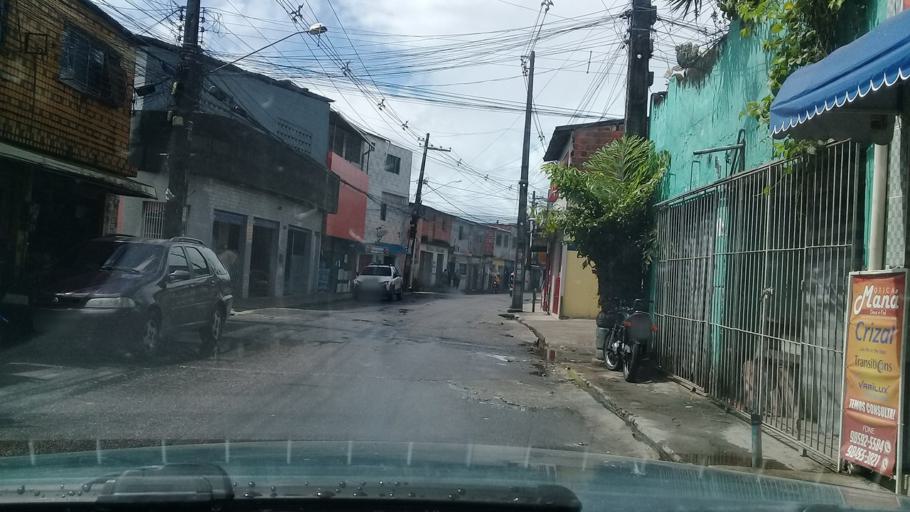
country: BR
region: Pernambuco
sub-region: Jaboatao Dos Guararapes
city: Jaboatao dos Guararapes
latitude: -8.1116
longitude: -34.9572
